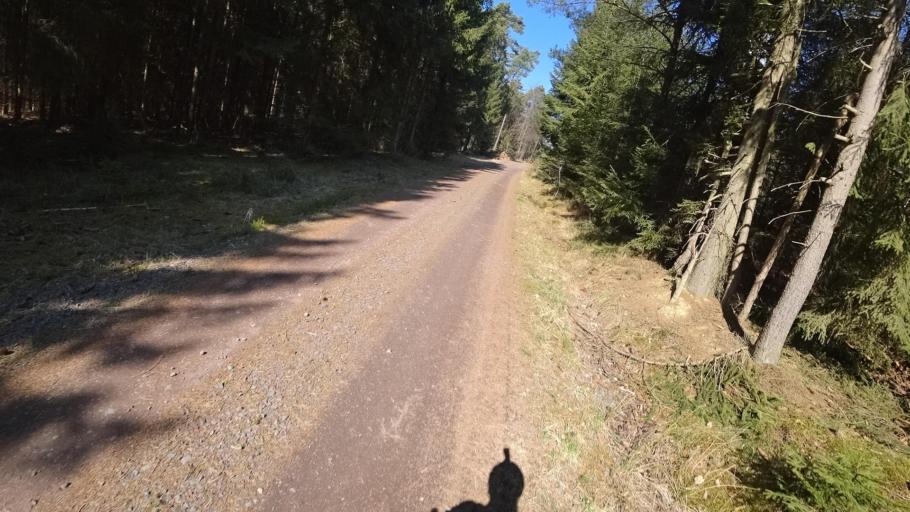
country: DE
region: Rheinland-Pfalz
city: Steinbach
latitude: 50.0307
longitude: 7.5897
